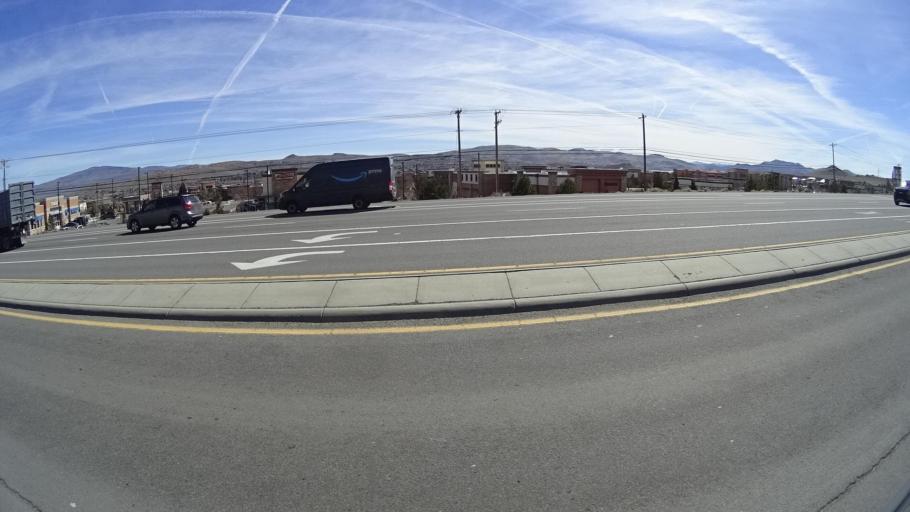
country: US
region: Nevada
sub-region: Washoe County
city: Sun Valley
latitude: 39.5826
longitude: -119.7437
